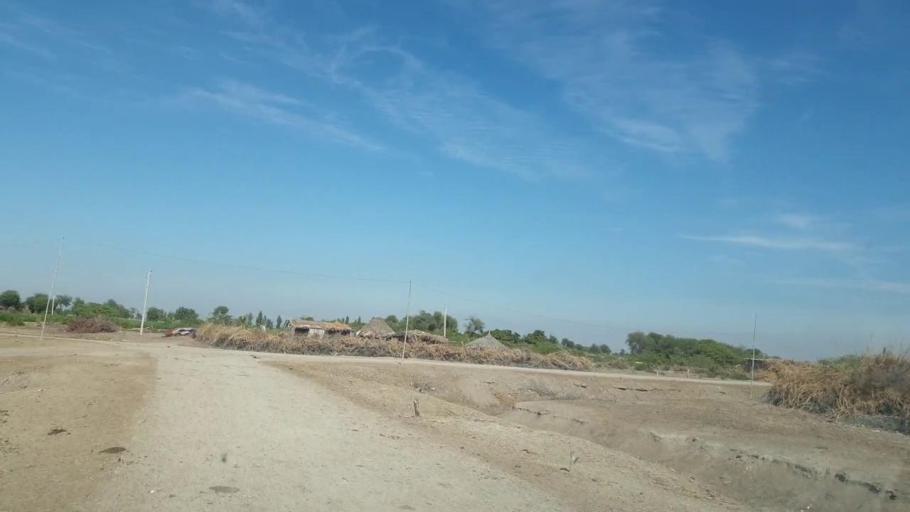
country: PK
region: Sindh
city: Pithoro
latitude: 25.6217
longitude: 69.2573
